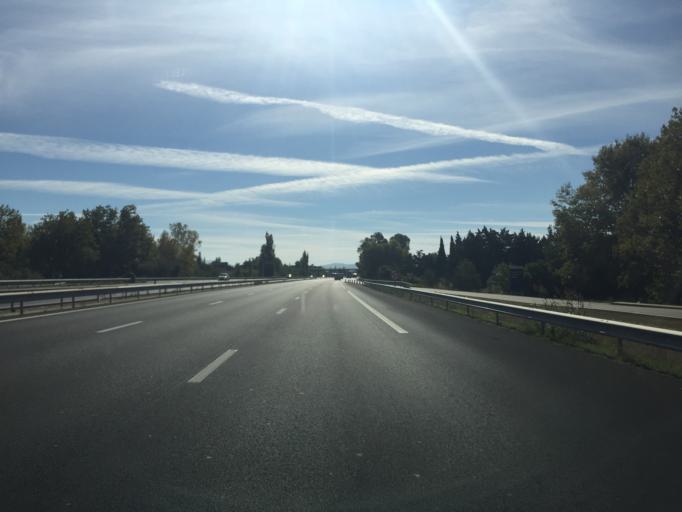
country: FR
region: Provence-Alpes-Cote d'Azur
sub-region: Departement des Bouches-du-Rhone
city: Senas
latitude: 43.7588
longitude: 5.0796
